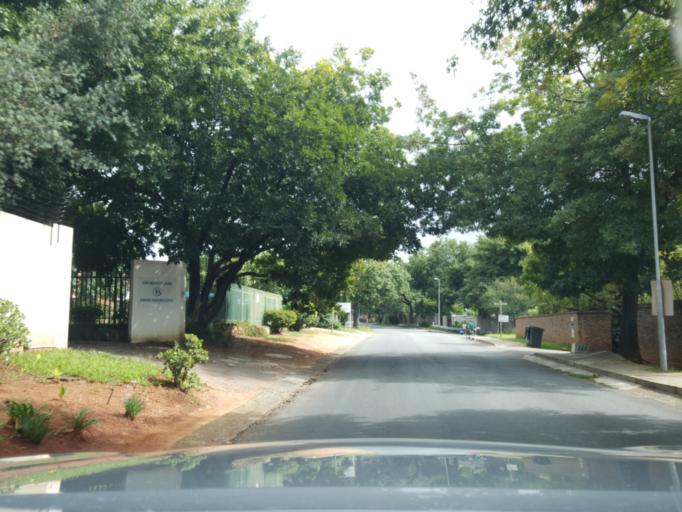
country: ZA
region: Gauteng
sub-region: City of Johannesburg Metropolitan Municipality
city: Johannesburg
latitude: -26.1116
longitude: 27.9988
